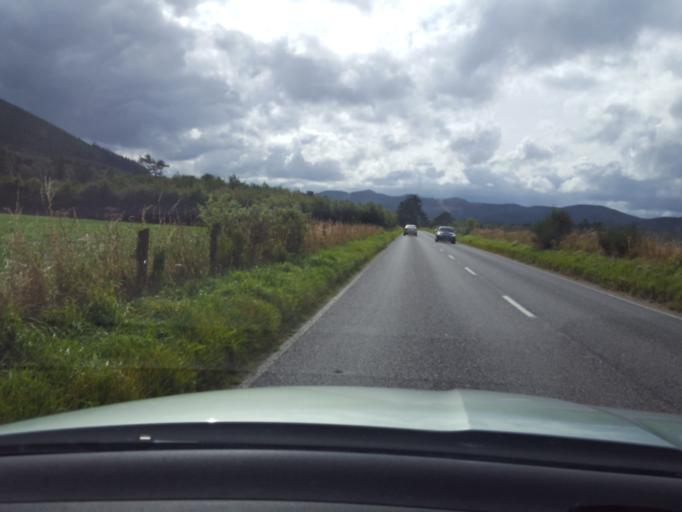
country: GB
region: Scotland
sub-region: Aberdeenshire
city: Ballater
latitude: 57.0578
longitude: -3.0235
